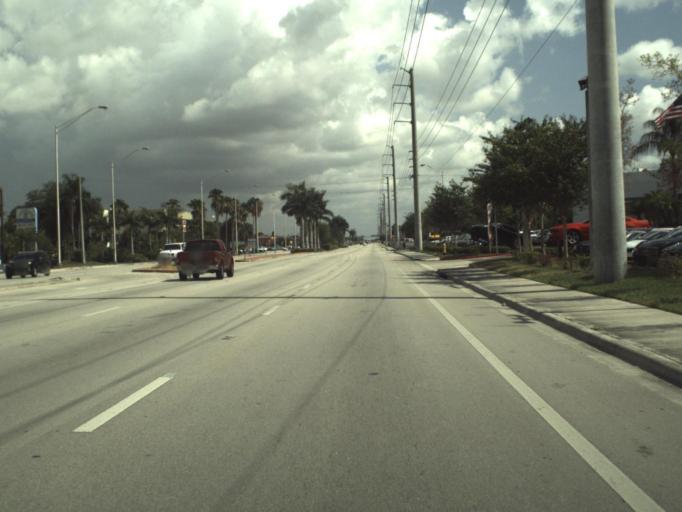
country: US
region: Florida
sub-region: Broward County
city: Miami Gardens
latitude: 25.9750
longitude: -80.2061
